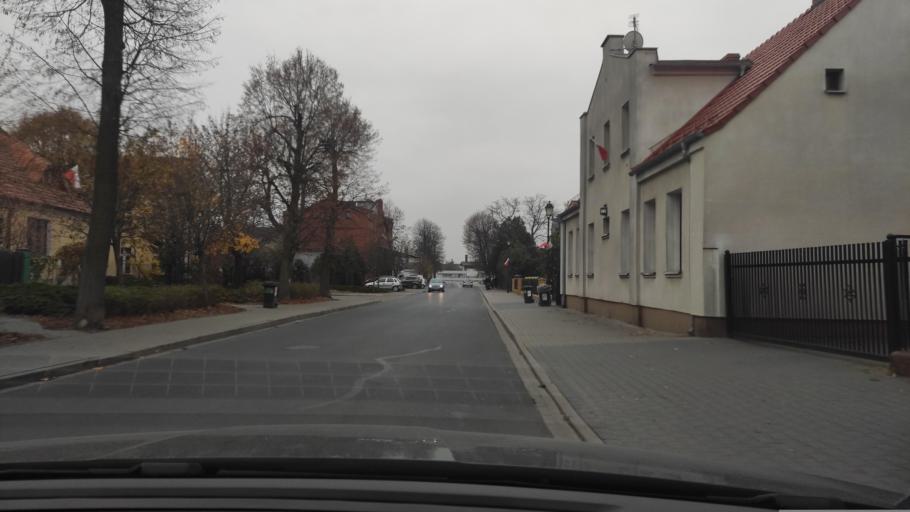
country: PL
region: Greater Poland Voivodeship
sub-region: Powiat poznanski
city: Kostrzyn
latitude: 52.3956
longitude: 17.2259
